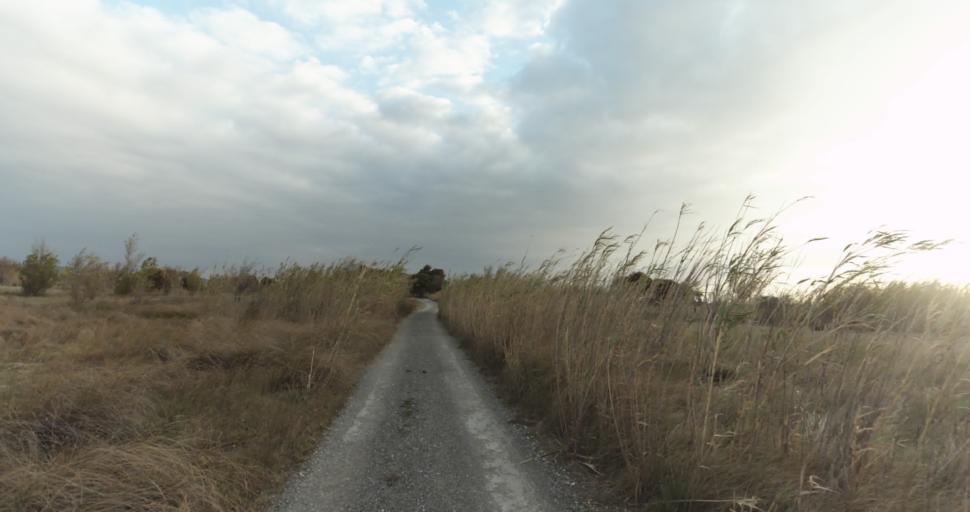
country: FR
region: Languedoc-Roussillon
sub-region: Departement de l'Aude
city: Leucate
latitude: 42.9498
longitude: 3.0317
